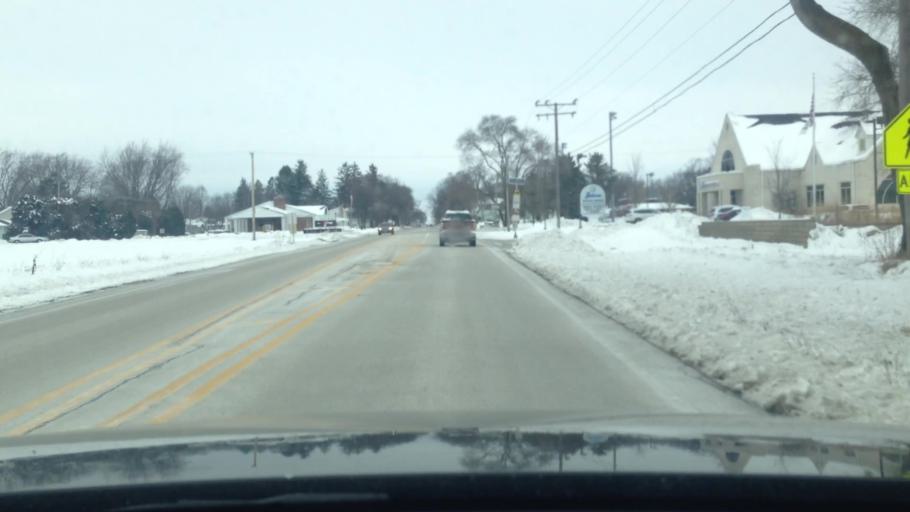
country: US
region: Illinois
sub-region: McHenry County
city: Hebron
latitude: 42.4638
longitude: -88.4329
